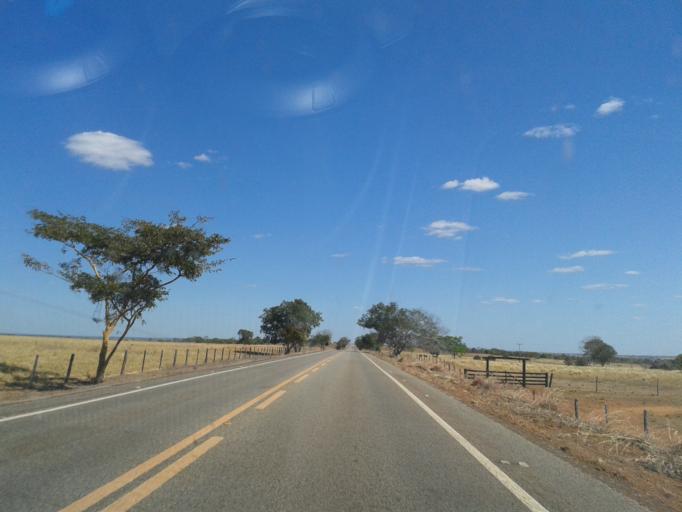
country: BR
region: Goias
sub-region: Sao Miguel Do Araguaia
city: Sao Miguel do Araguaia
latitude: -13.4046
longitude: -50.2613
